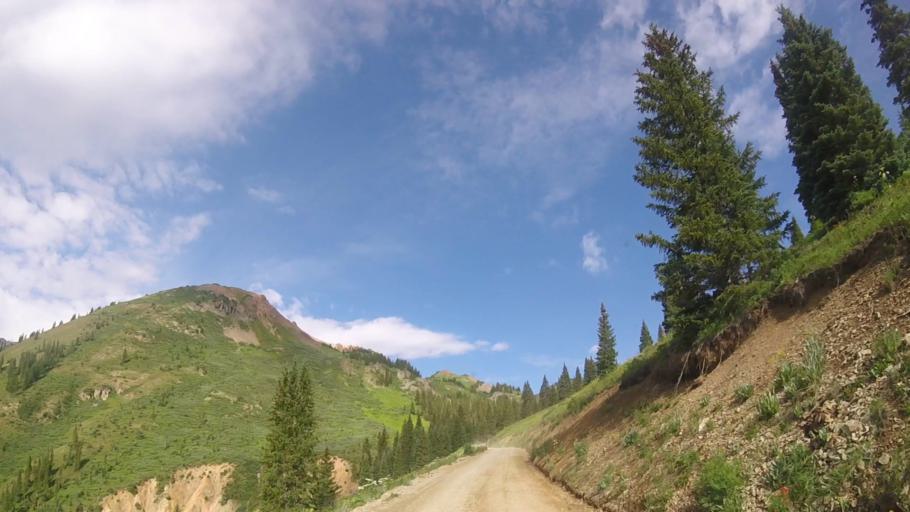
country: US
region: Colorado
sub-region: San Miguel County
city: Telluride
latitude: 37.8459
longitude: -107.7665
